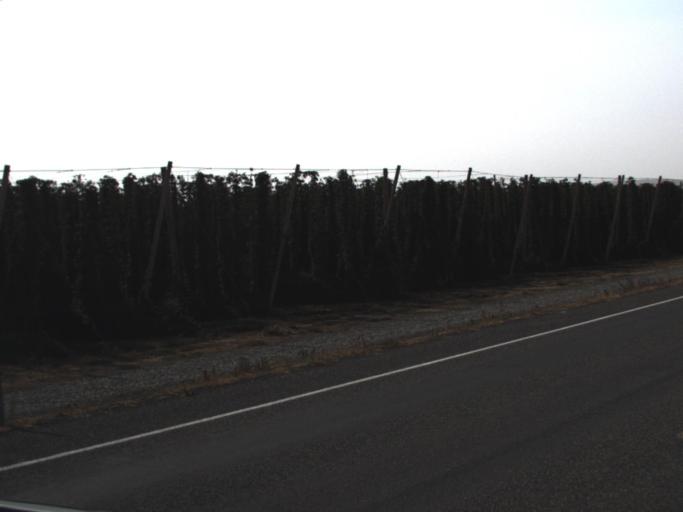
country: US
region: Washington
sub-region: Yakima County
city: Granger
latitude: 46.2843
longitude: -120.1709
